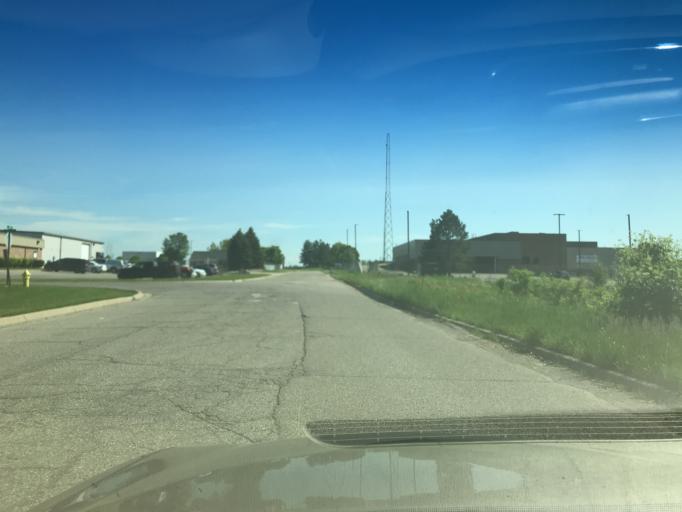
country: US
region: Michigan
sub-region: Eaton County
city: Waverly
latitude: 42.7044
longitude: -84.6674
